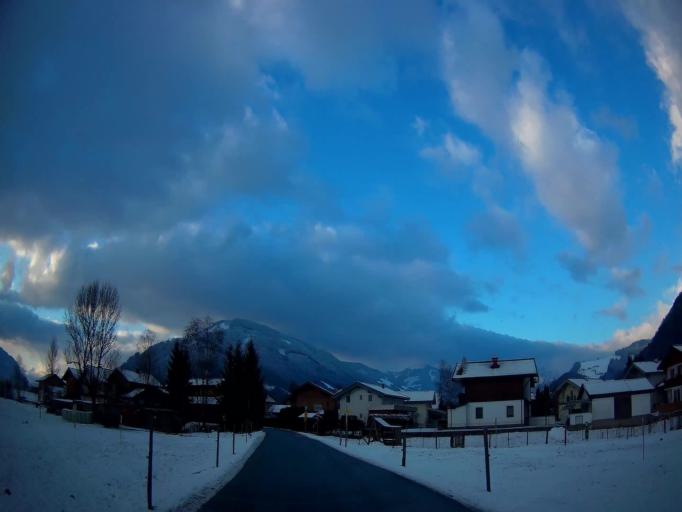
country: AT
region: Salzburg
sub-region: Politischer Bezirk Zell am See
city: Saalfelden am Steinernen Meer
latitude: 47.4517
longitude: 12.8206
